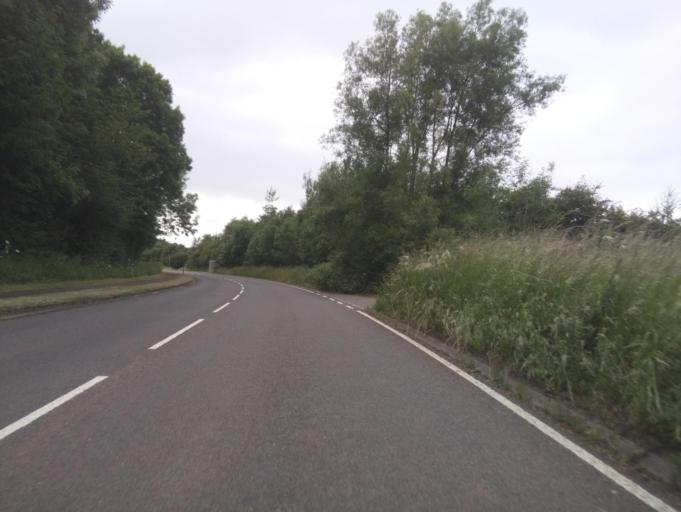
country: GB
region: England
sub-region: Staffordshire
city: Uttoxeter
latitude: 52.8911
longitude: -1.7684
